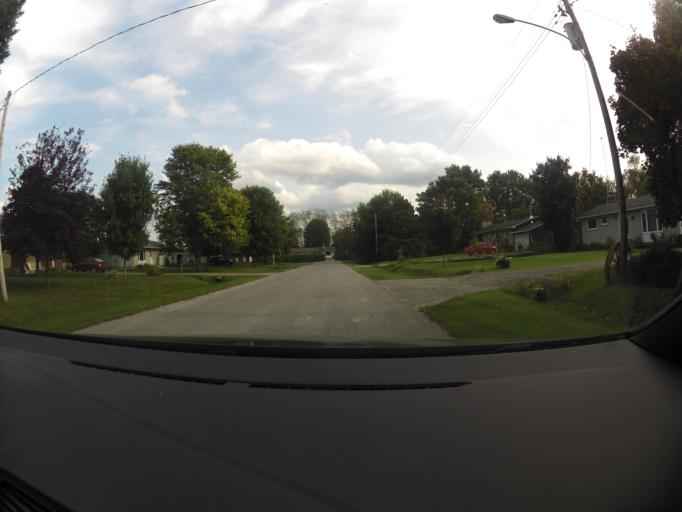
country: CA
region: Ontario
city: Carleton Place
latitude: 45.3599
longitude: -76.1222
